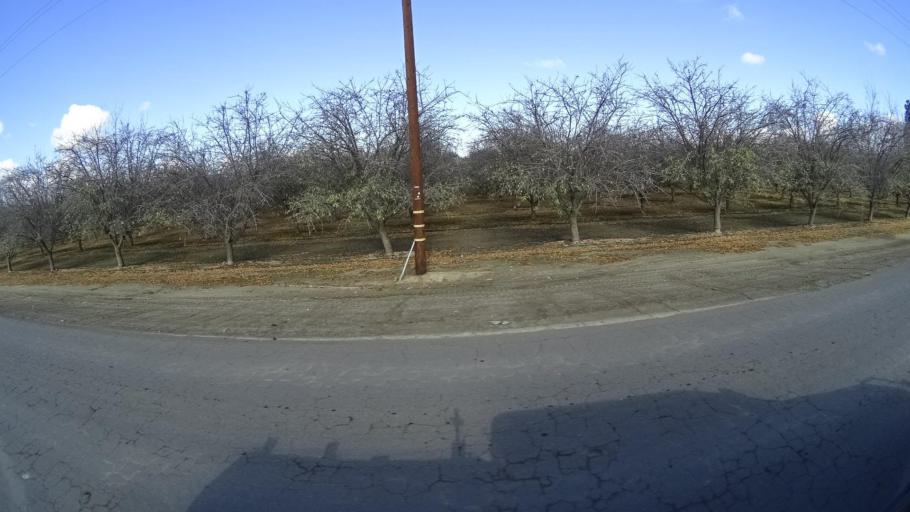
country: US
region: California
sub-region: Kern County
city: McFarland
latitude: 35.6887
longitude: -119.2836
